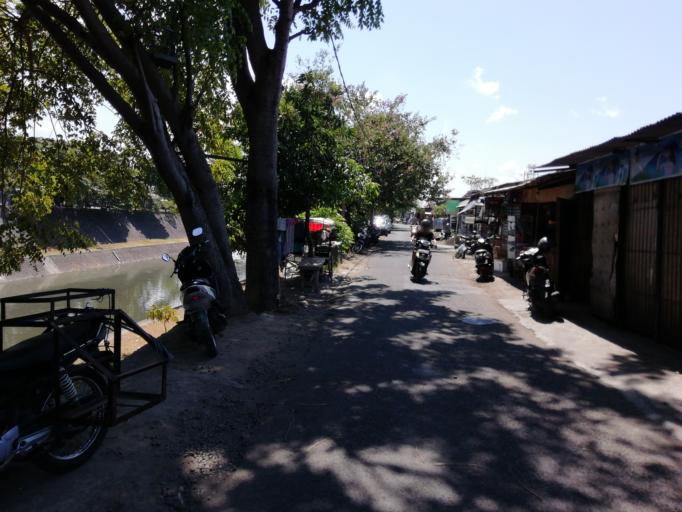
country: ID
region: Bali
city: Karyadharma
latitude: -8.6912
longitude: 115.1976
